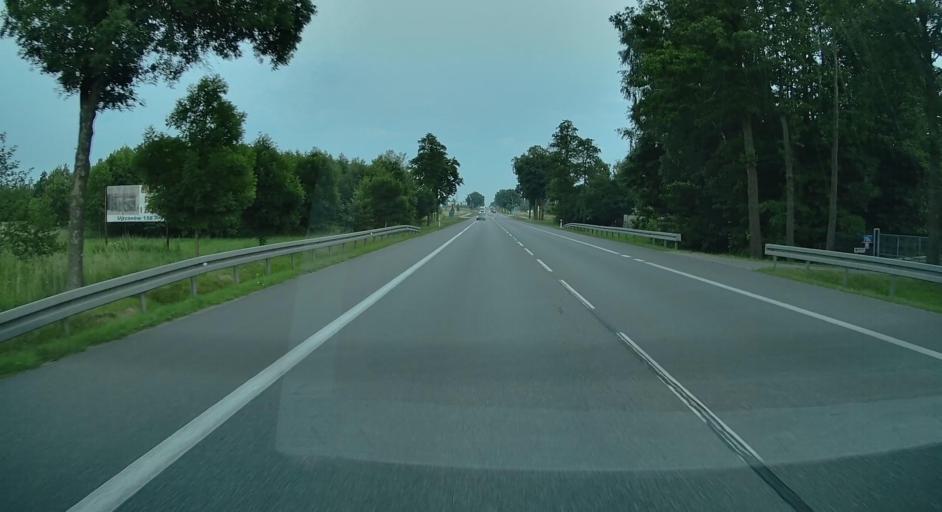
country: PL
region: Masovian Voivodeship
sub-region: Siedlce
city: Siedlce
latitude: 52.1297
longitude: 22.3352
